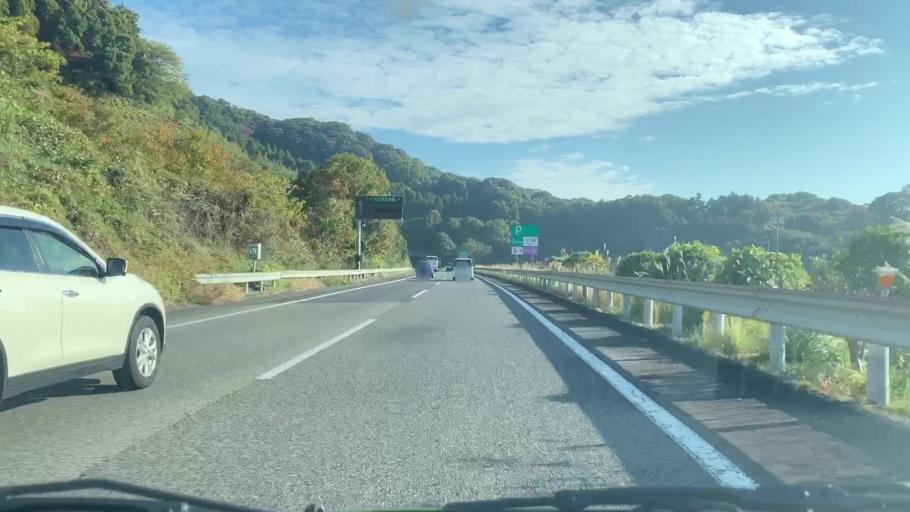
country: JP
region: Saga Prefecture
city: Saga-shi
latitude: 33.3008
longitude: 130.1856
